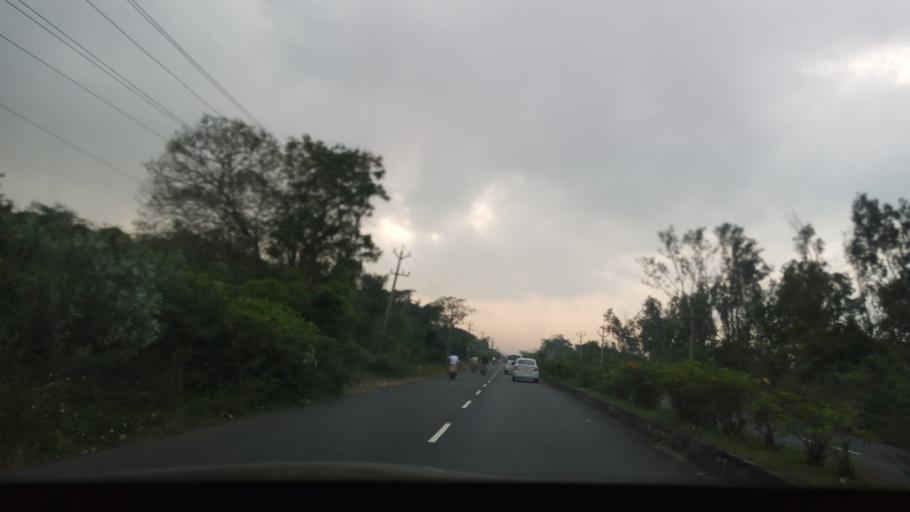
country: IN
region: Tamil Nadu
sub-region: Kancheepuram
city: Vengavasal
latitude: 12.8180
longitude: 80.1757
